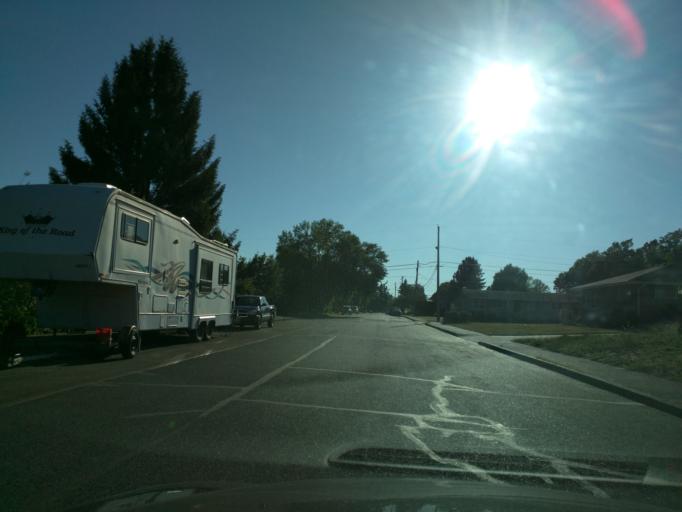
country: US
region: Washington
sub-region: Whatcom County
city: Lynden
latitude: 48.9388
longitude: -122.4655
